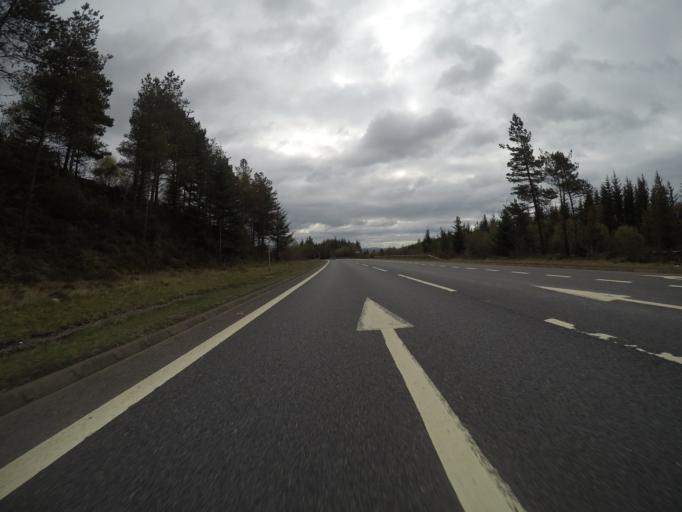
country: GB
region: Scotland
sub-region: Highland
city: Kingussie
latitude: 56.8071
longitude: -4.0944
